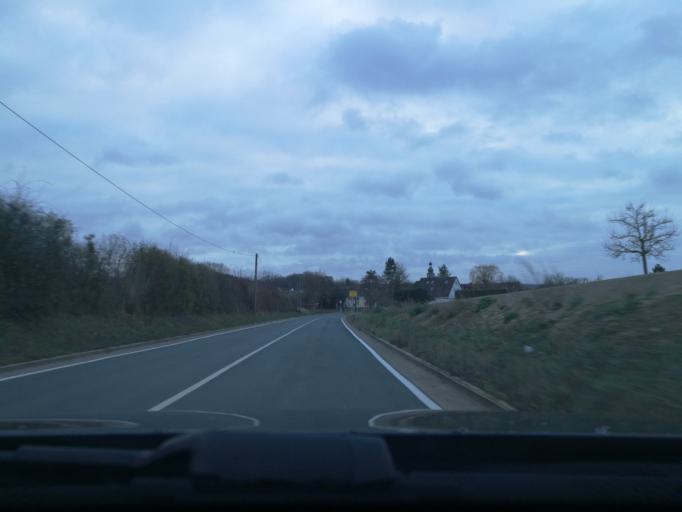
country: DE
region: Bavaria
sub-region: Regierungsbezirk Mittelfranken
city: Uttenreuth
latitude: 49.6034
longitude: 11.0759
